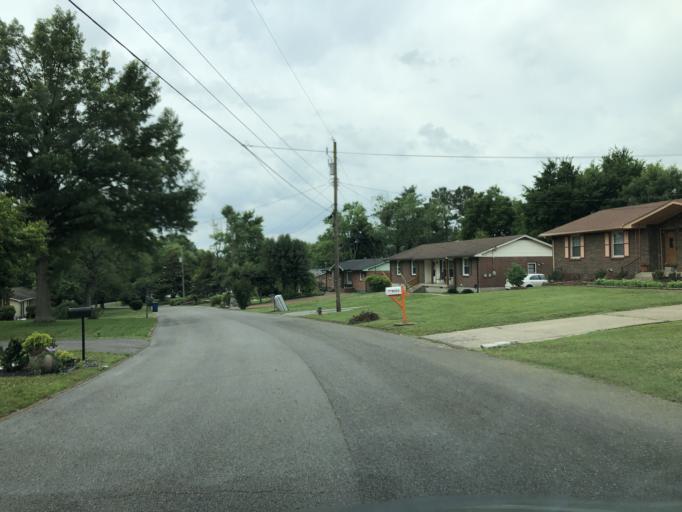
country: US
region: Tennessee
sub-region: Davidson County
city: Goodlettsville
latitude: 36.2924
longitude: -86.7125
